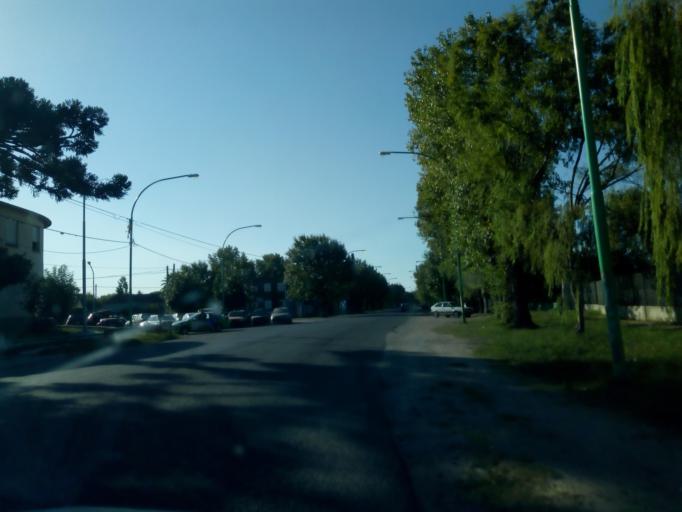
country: AR
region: Buenos Aires
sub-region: Partido de Ensenada
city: Ensenada
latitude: -34.8130
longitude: -57.9798
